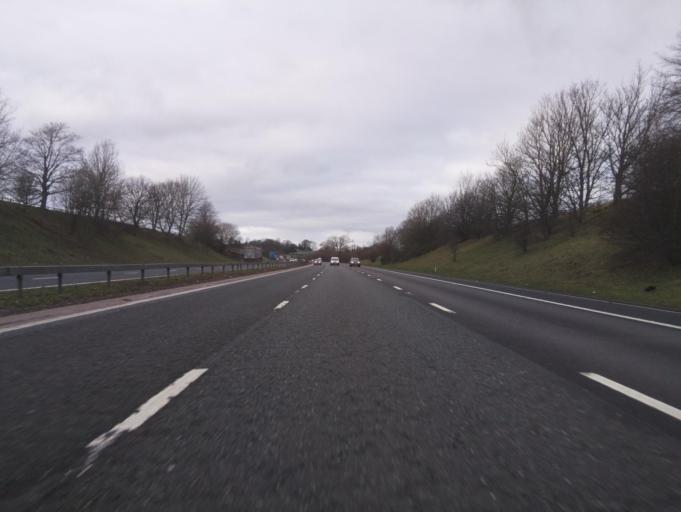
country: GB
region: England
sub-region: Cumbria
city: Carlisle
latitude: 54.9253
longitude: -2.9124
